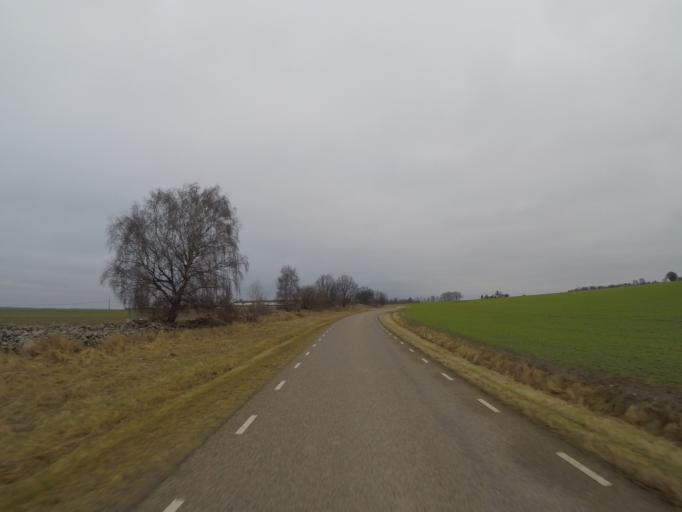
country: SE
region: Skane
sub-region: Hoors Kommun
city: Loberod
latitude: 55.7888
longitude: 13.4003
